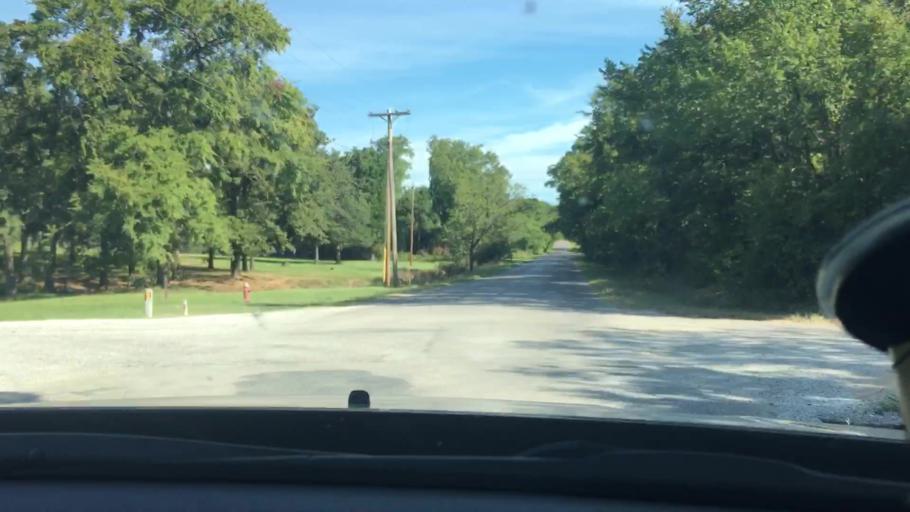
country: US
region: Oklahoma
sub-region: Carter County
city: Lone Grove
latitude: 34.2164
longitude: -97.2474
